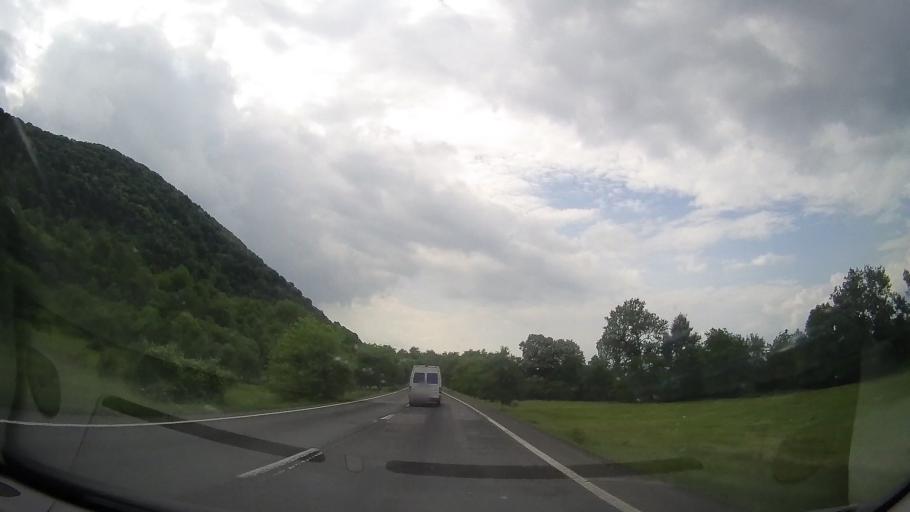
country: RO
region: Hunedoara
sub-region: Comuna Branisca
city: Branisca
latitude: 45.9180
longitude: 22.7242
